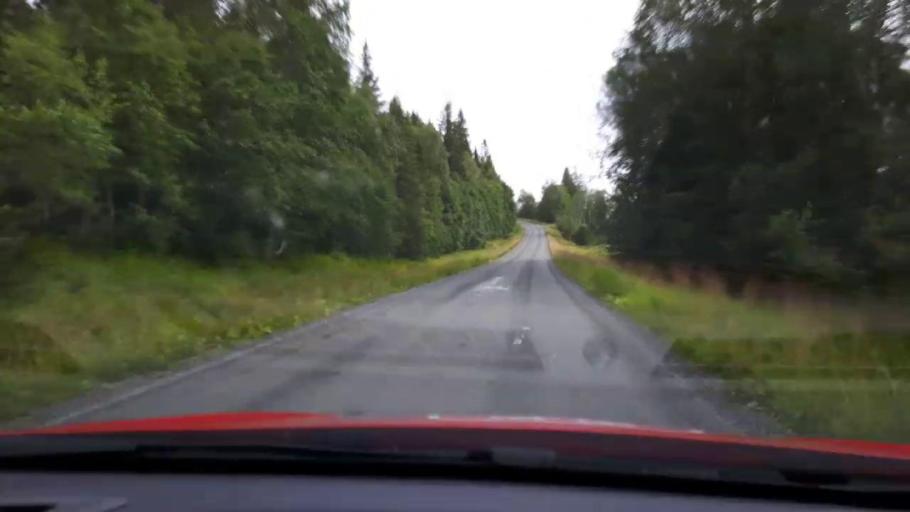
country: SE
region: Jaemtland
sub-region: Are Kommun
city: Are
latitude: 63.7409
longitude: 13.0049
